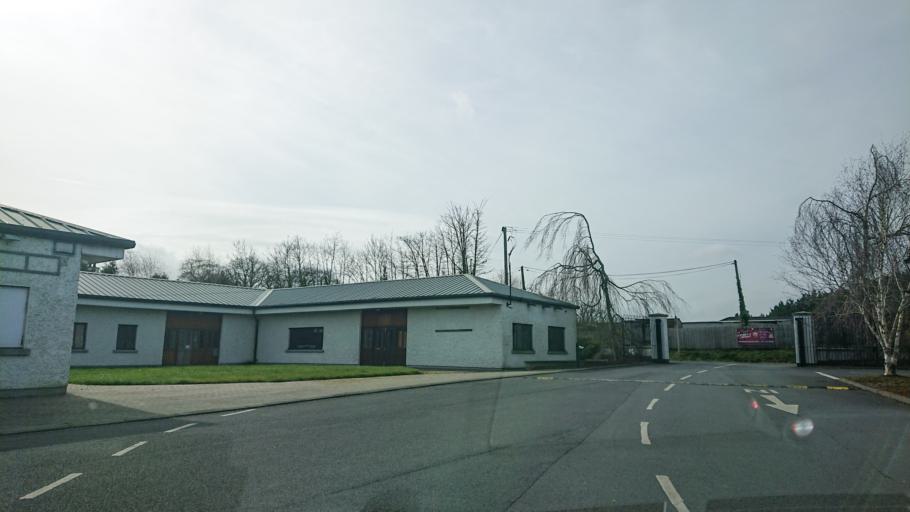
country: IE
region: Leinster
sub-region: County Carlow
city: Bagenalstown
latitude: 52.7426
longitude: -6.9756
